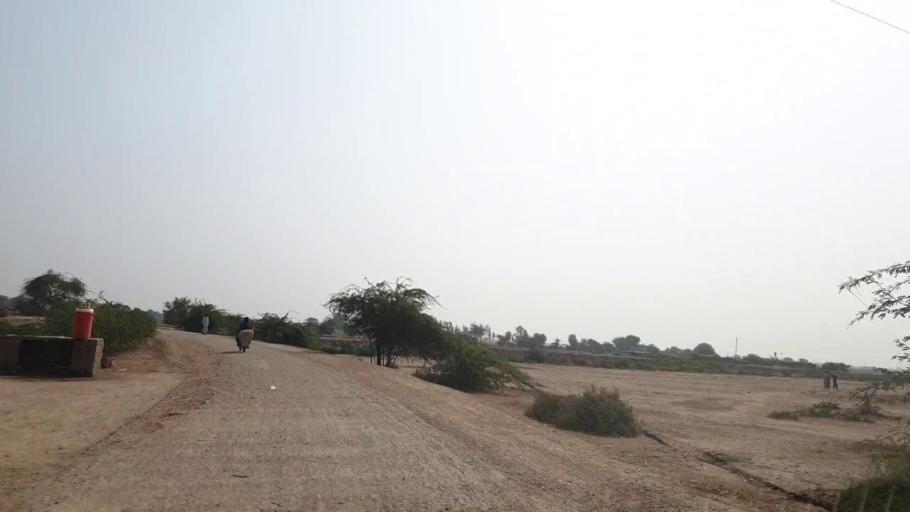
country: PK
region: Sindh
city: Matli
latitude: 24.9987
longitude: 68.5735
